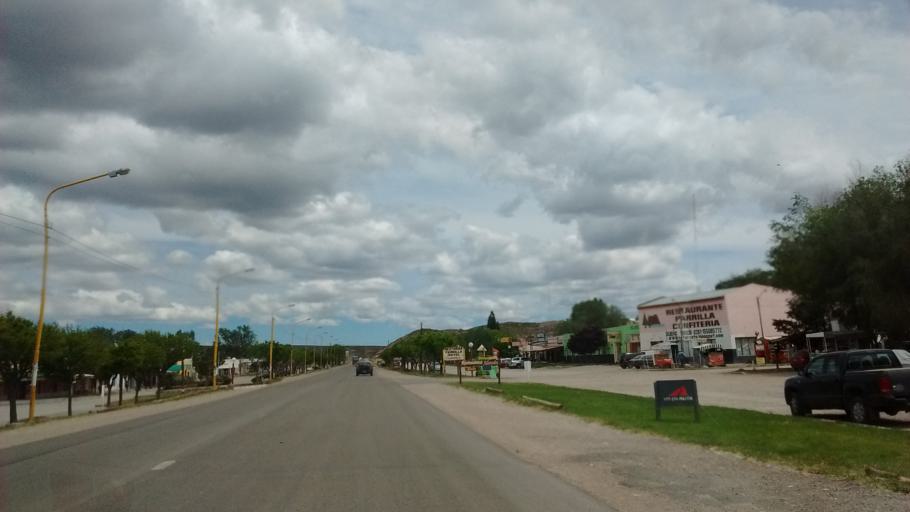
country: AR
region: Neuquen
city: Piedra del Aguila
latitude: -40.0487
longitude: -70.0768
